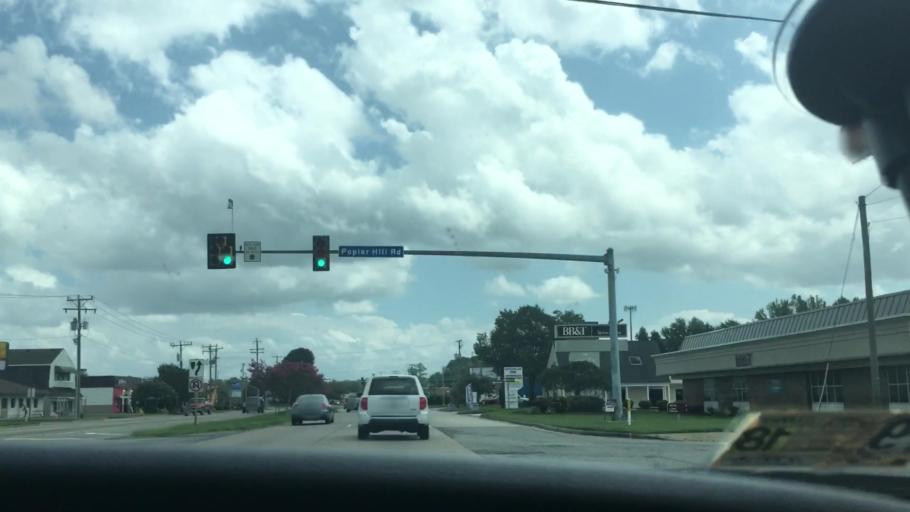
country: US
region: Virginia
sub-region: City of Portsmouth
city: Portsmouth Heights
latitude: 36.8622
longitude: -76.4014
